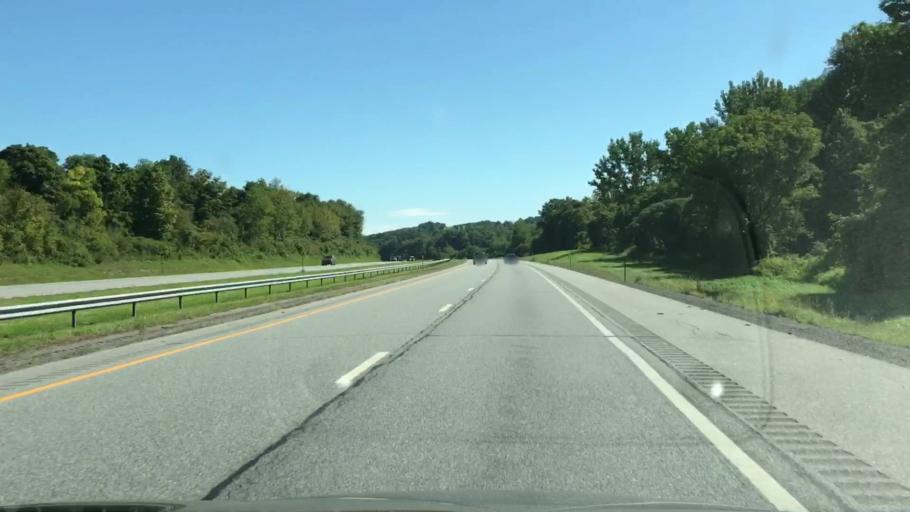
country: US
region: New York
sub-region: Montgomery County
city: Saint Johnsville
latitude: 42.9903
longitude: -74.7283
